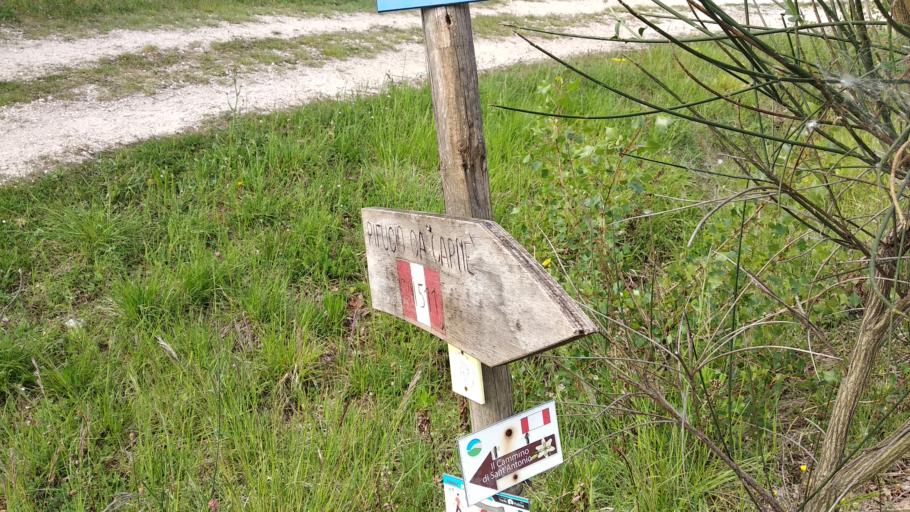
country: IT
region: Emilia-Romagna
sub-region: Provincia di Ravenna
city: Brisighella
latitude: 44.2242
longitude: 11.7603
